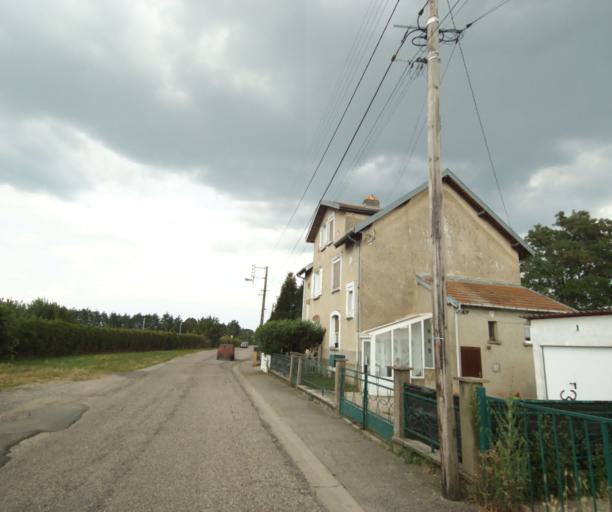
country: FR
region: Lorraine
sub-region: Departement de Meurthe-et-Moselle
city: Chanteheux
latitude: 48.5879
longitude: 6.5164
